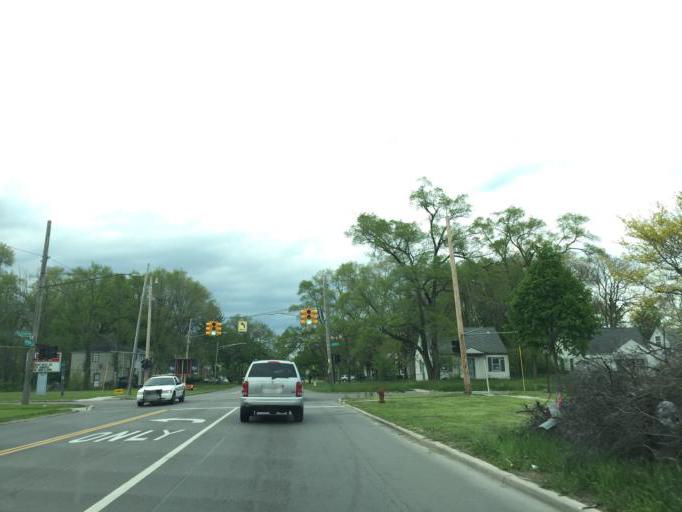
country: US
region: Michigan
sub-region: Wayne County
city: Redford
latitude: 42.3930
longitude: -83.2371
